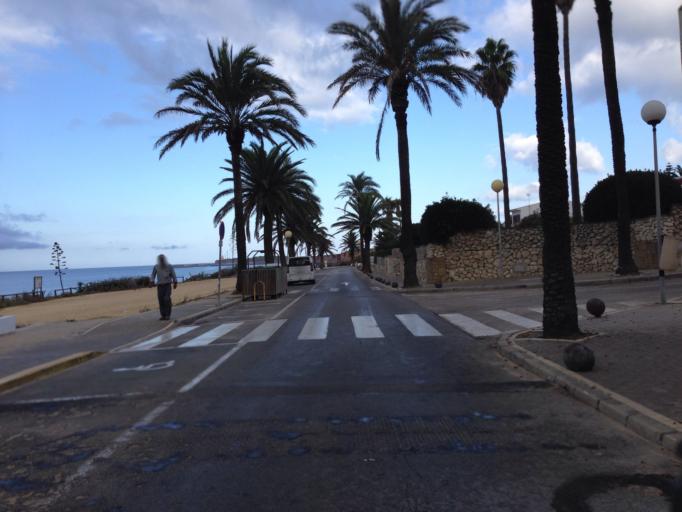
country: ES
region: Andalusia
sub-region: Provincia de Cadiz
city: Conil de la Frontera
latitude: 36.2906
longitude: -6.1081
